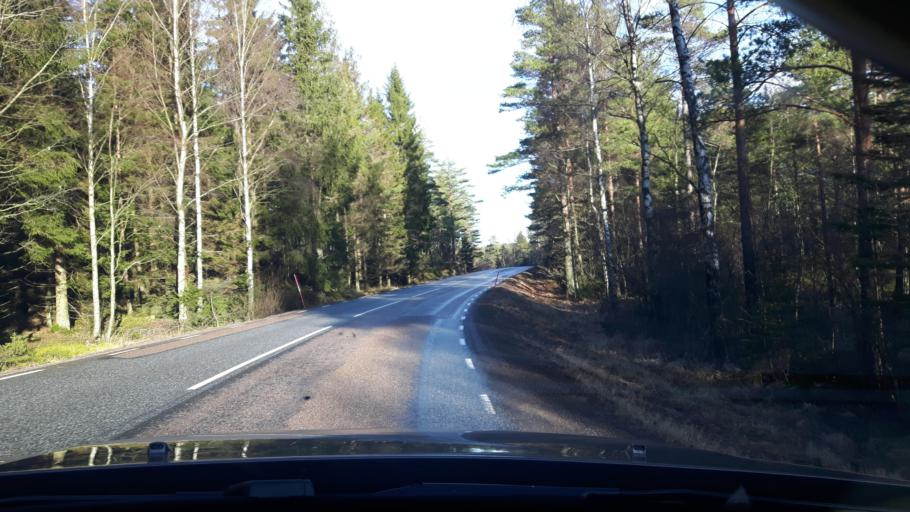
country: SE
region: Vaestra Goetaland
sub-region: Munkedals Kommun
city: Munkedal
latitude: 58.5065
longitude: 11.6814
